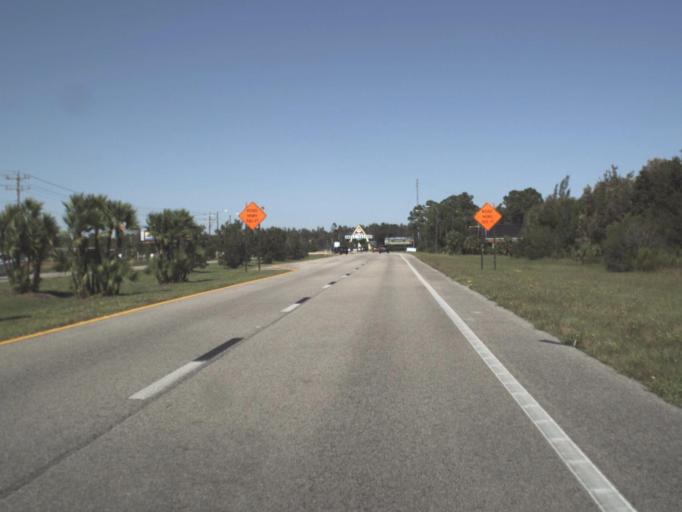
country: US
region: Florida
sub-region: Lee County
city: Palmona Park
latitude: 26.7006
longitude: -81.9002
